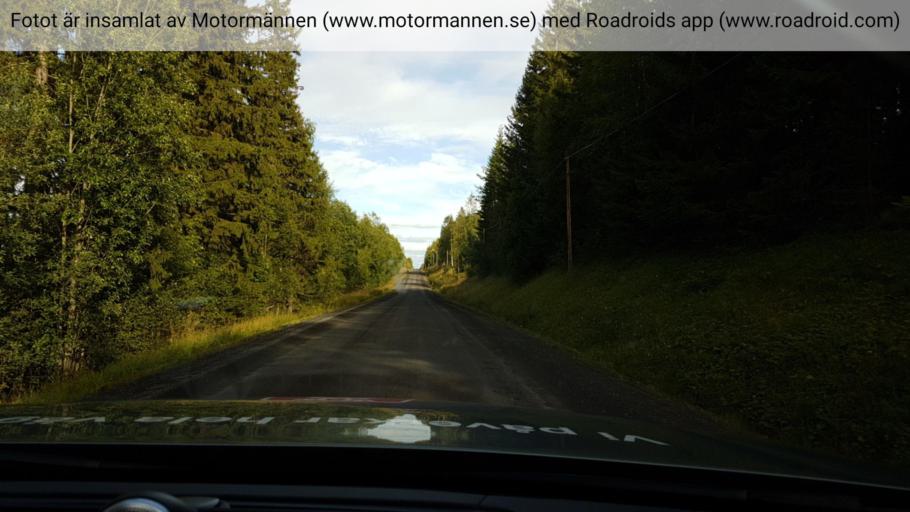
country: SE
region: Jaemtland
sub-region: Stroemsunds Kommun
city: Stroemsund
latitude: 64.1433
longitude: 15.7052
